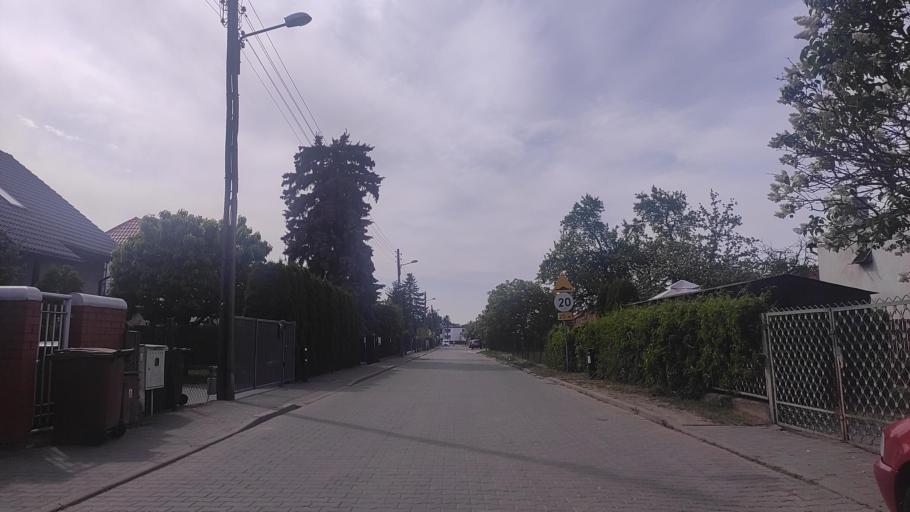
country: PL
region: Greater Poland Voivodeship
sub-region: Powiat poznanski
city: Swarzedz
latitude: 52.4105
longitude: 17.0958
